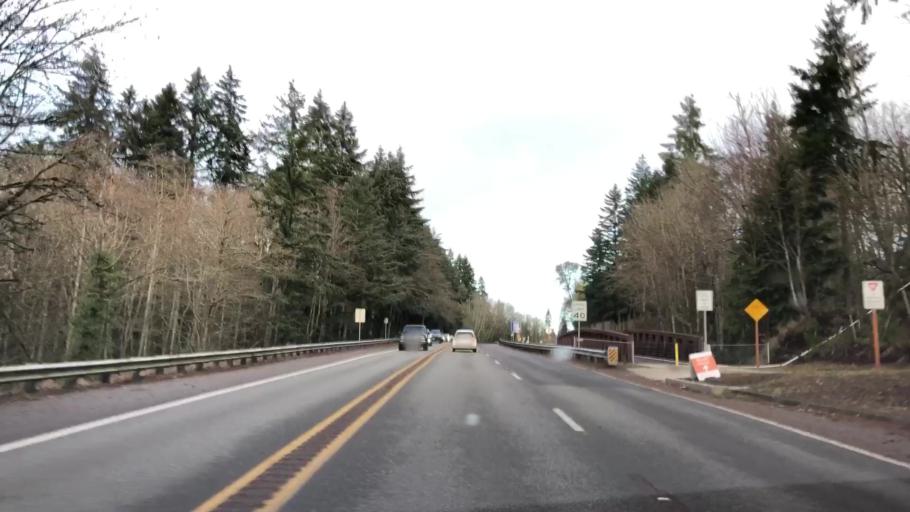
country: US
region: Washington
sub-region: Kitsap County
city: Bainbridge Island
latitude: 47.6280
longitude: -122.5149
